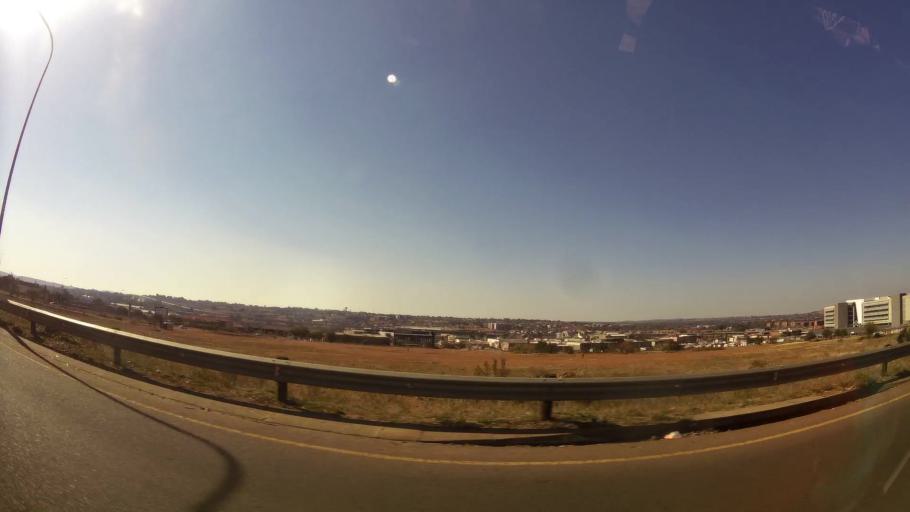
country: ZA
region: Gauteng
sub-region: City of Tshwane Metropolitan Municipality
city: Centurion
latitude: -25.8599
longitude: 28.1812
